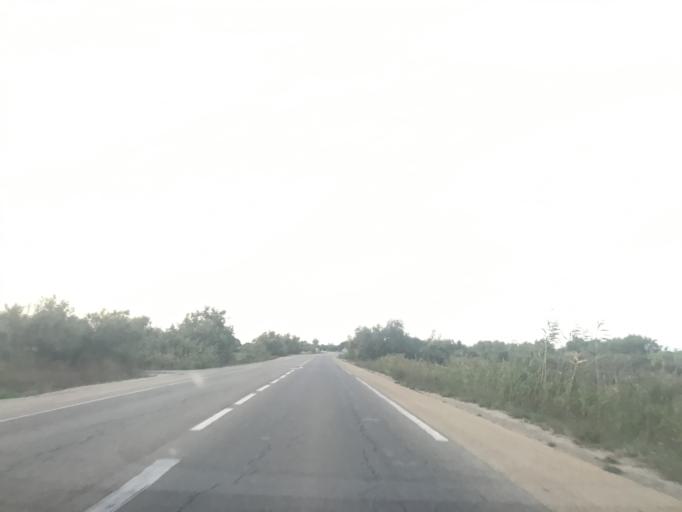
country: FR
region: Provence-Alpes-Cote d'Azur
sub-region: Departement des Bouches-du-Rhone
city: Saintes-Maries-de-la-Mer
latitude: 43.4829
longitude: 4.4046
